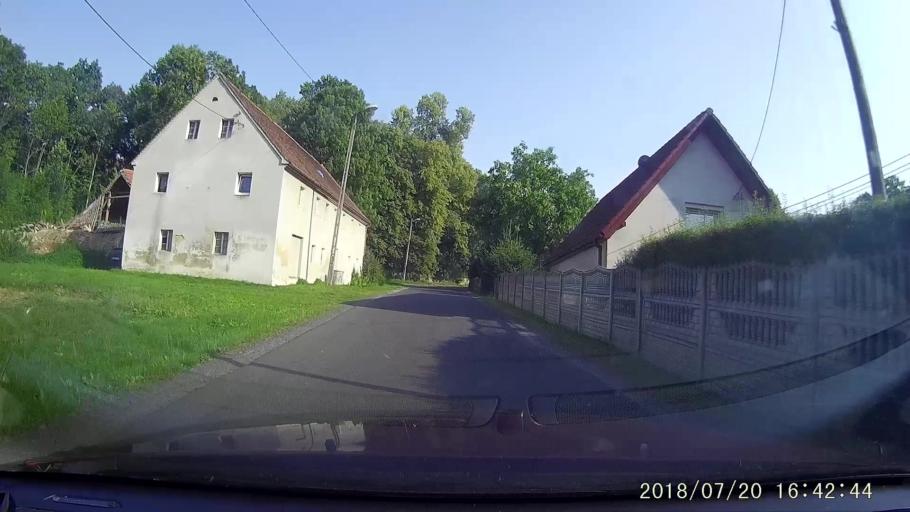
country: PL
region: Lower Silesian Voivodeship
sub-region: Powiat lubanski
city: Siekierczyn
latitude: 51.0737
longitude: 15.1559
